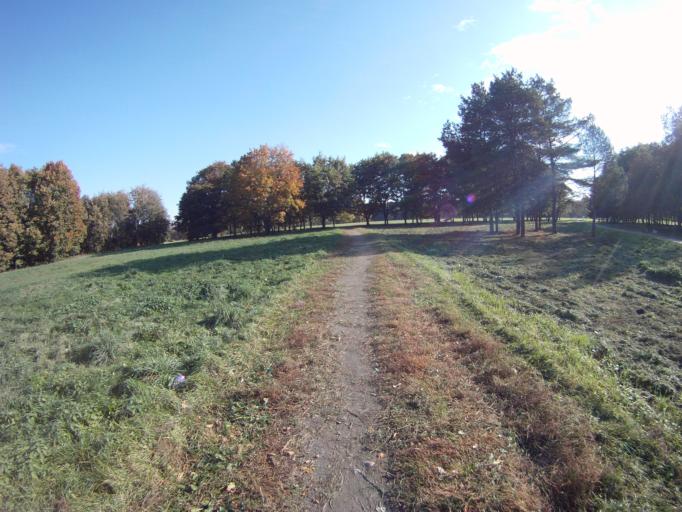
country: BY
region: Minsk
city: Minsk
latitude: 53.9370
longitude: 27.5678
